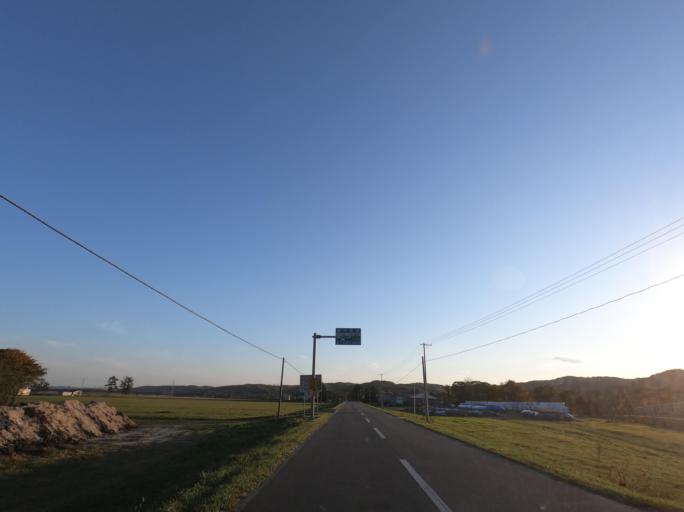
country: JP
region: Hokkaido
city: Kushiro
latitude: 43.2016
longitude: 144.4250
